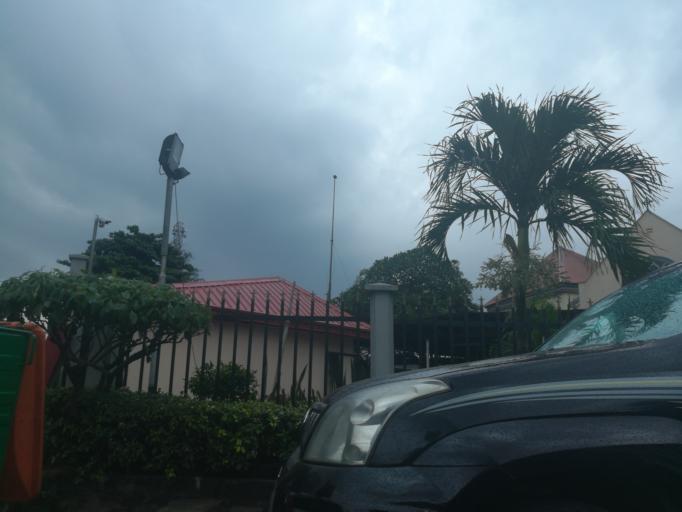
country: NG
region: Lagos
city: Lagos
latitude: 6.4469
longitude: 3.3986
